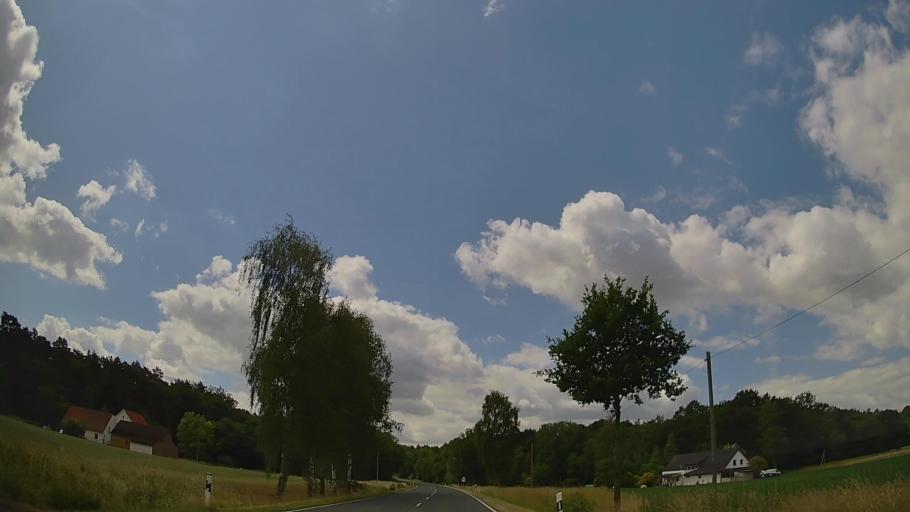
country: DE
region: North Rhine-Westphalia
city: Rahden
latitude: 52.4061
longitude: 8.5195
